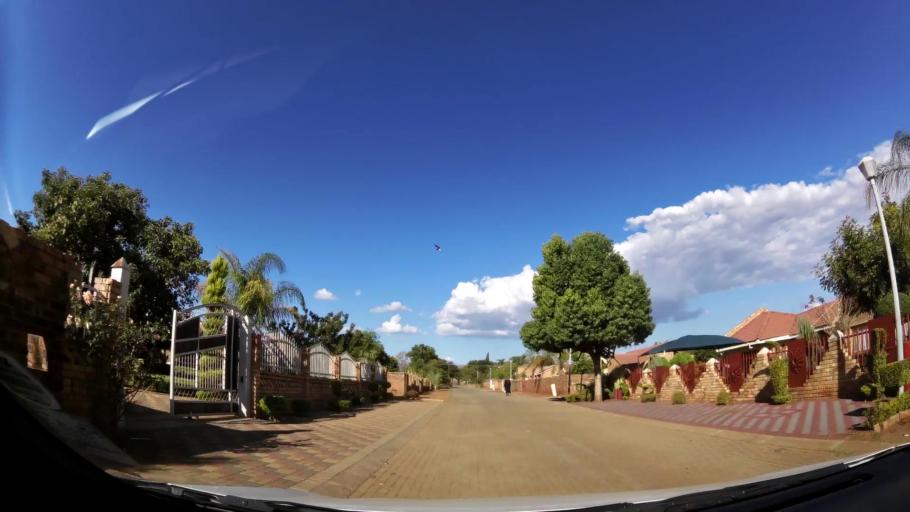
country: ZA
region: Limpopo
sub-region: Waterberg District Municipality
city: Mokopane
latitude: -24.1760
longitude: 28.9944
